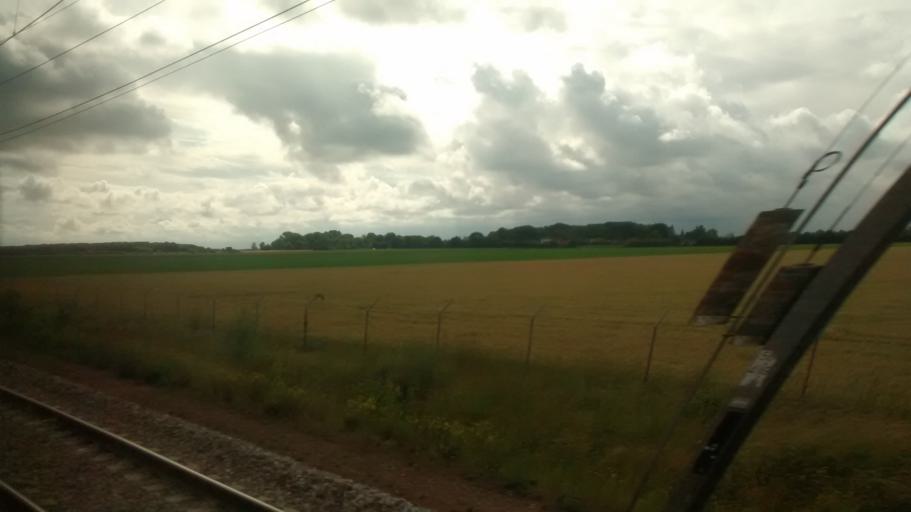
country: FR
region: Ile-de-France
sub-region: Departement des Yvelines
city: Ablis
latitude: 48.4724
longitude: 1.8470
